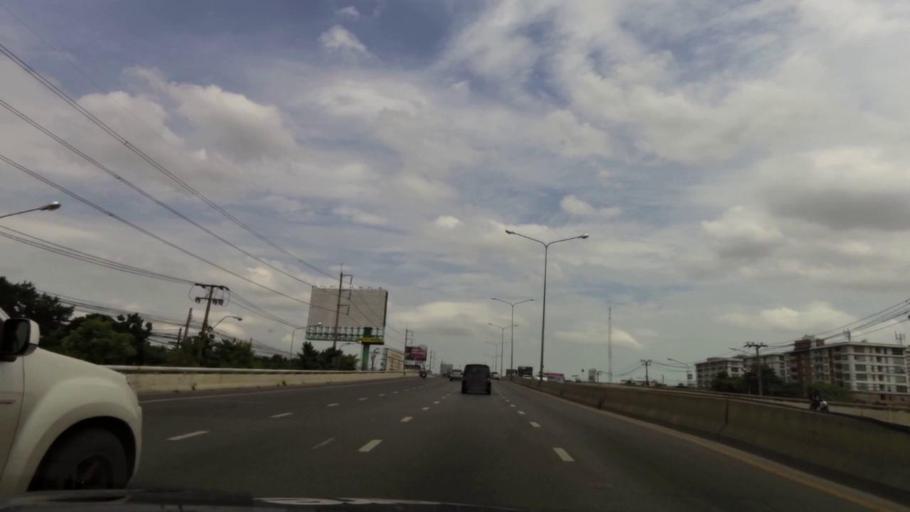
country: TH
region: Bangkok
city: Suan Luang
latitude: 13.7169
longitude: 100.6428
